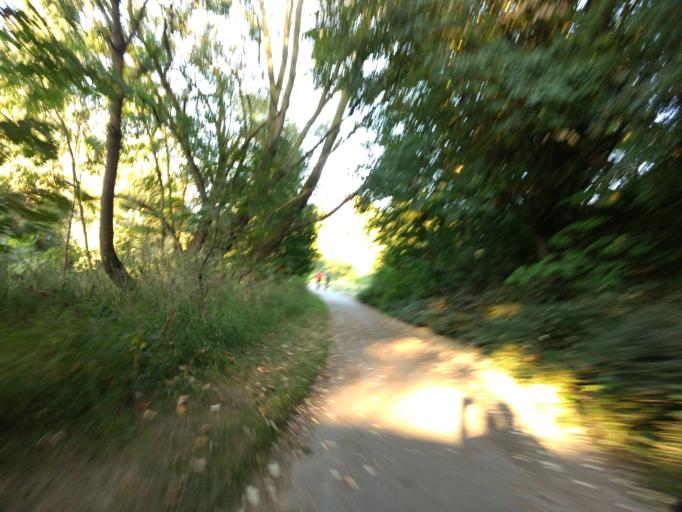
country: DE
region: Saarland
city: Rehlingen-Siersburg
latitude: 49.3560
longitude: 6.6131
